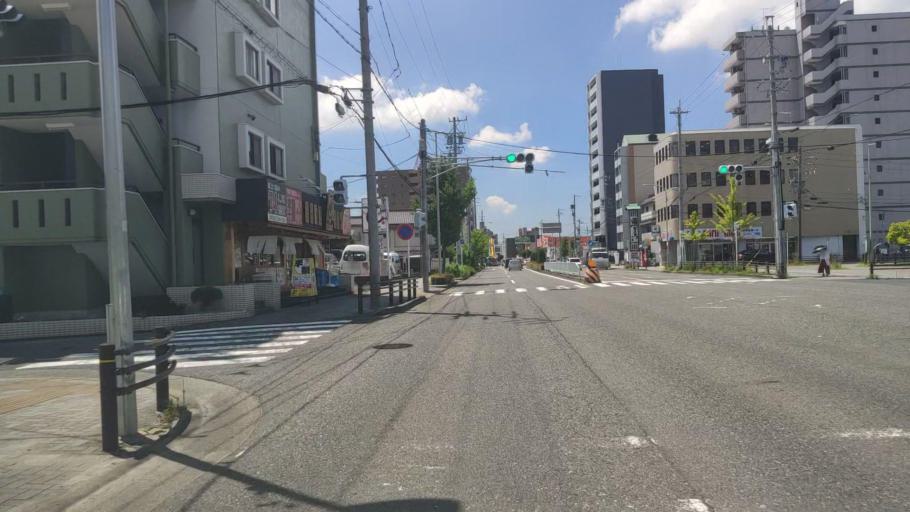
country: JP
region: Aichi
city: Kanie
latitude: 35.1484
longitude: 136.8533
